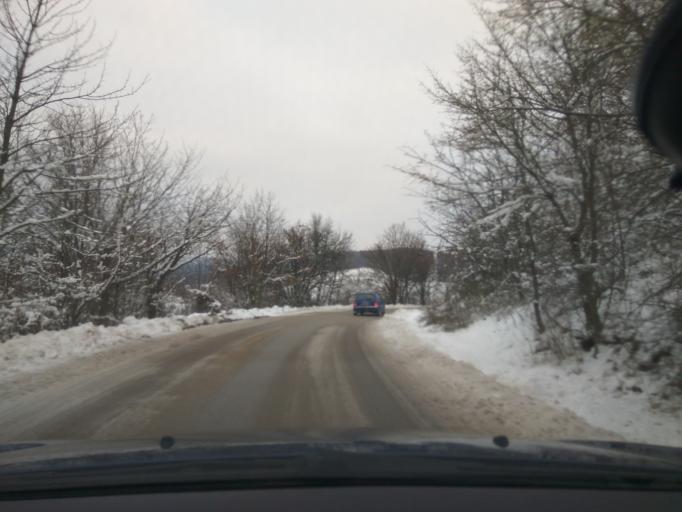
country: SK
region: Nitriansky
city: Stara Tura
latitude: 48.8312
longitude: 17.7048
